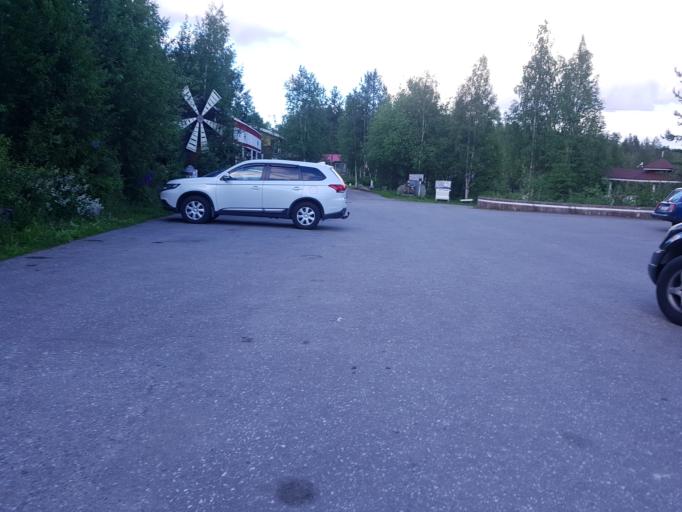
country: RU
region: Republic of Karelia
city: Kostomuksha
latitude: 64.6028
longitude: 30.5754
